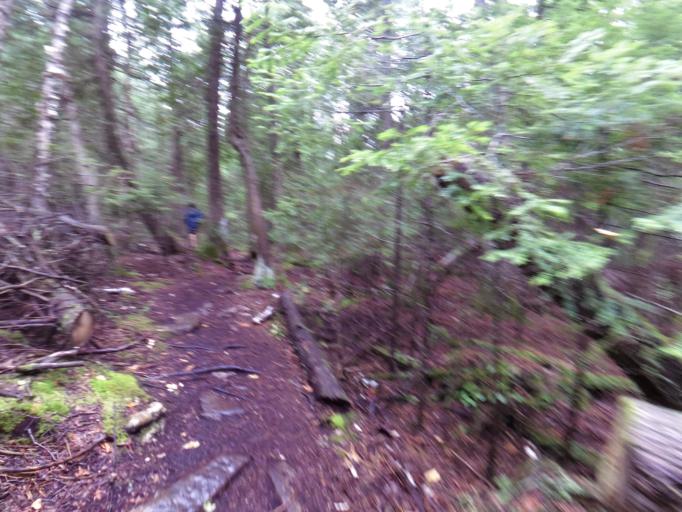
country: CA
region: Ontario
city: Tobermory
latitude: 45.2617
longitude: -81.6462
